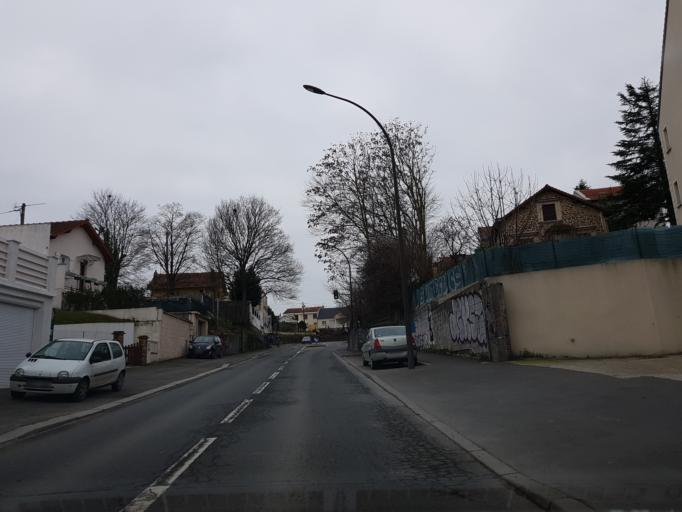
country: FR
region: Ile-de-France
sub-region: Departement du Val-de-Marne
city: Villejuif
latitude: 48.7895
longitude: 2.3789
